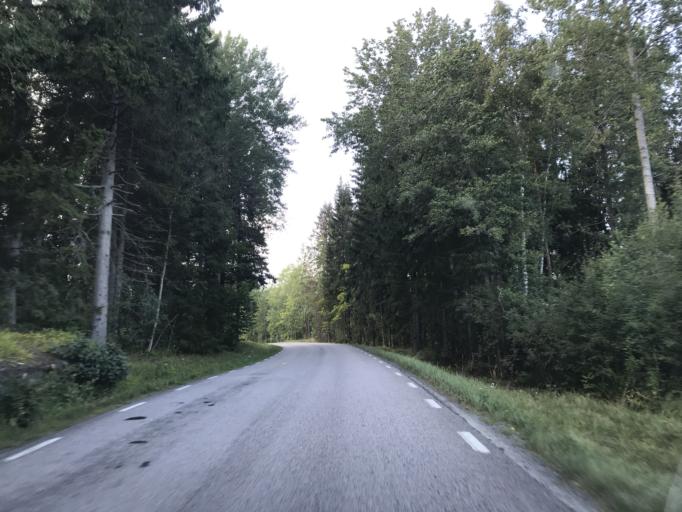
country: SE
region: Stockholm
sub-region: Norrtalje Kommun
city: Bjorko
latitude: 59.8690
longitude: 19.0168
